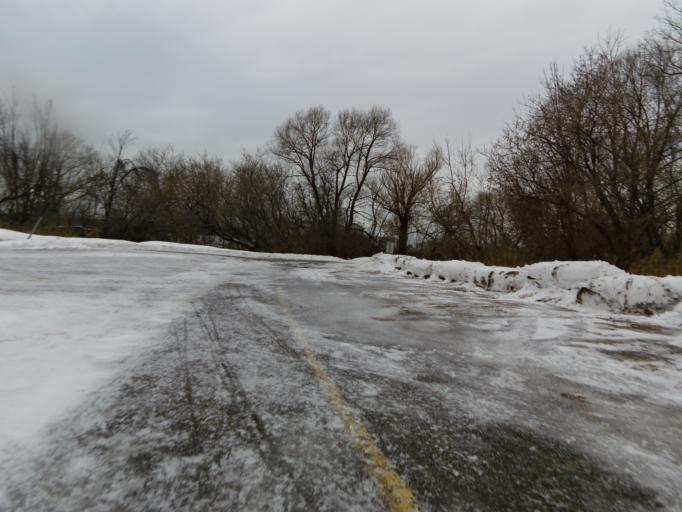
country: CA
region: Ontario
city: Ottawa
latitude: 45.4140
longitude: -75.6647
